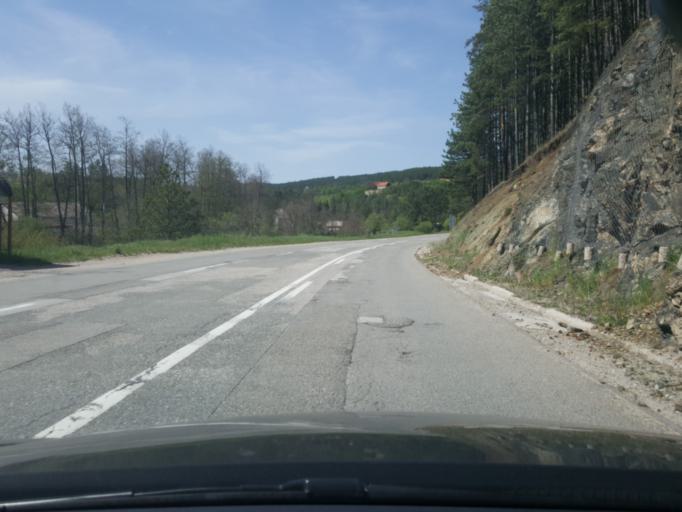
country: RS
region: Central Serbia
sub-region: Zlatiborski Okrug
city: Bajina Basta
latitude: 43.8381
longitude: 19.6056
